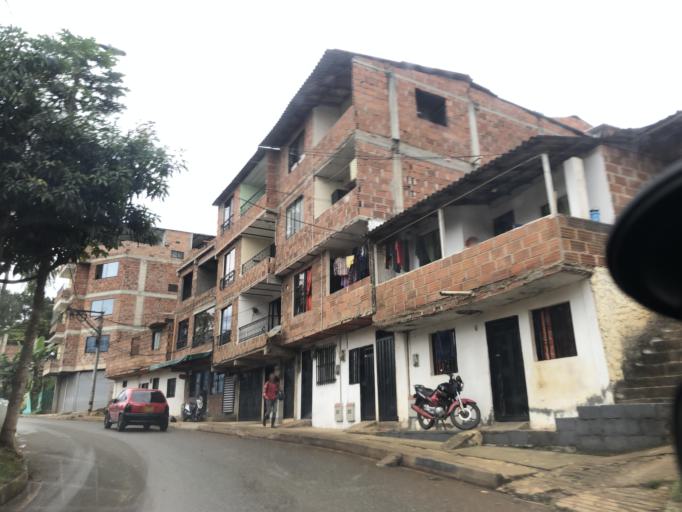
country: CO
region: Antioquia
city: Bello
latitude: 6.3264
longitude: -75.5449
